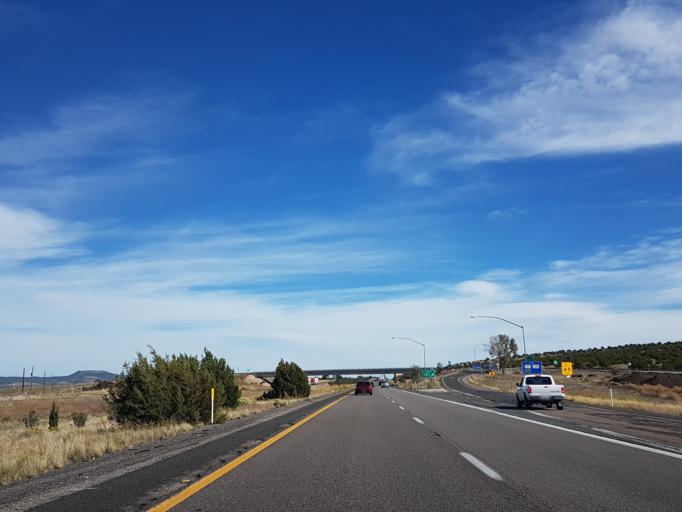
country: US
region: Arizona
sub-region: Mohave County
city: Peach Springs
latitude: 35.3206
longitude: -112.8967
